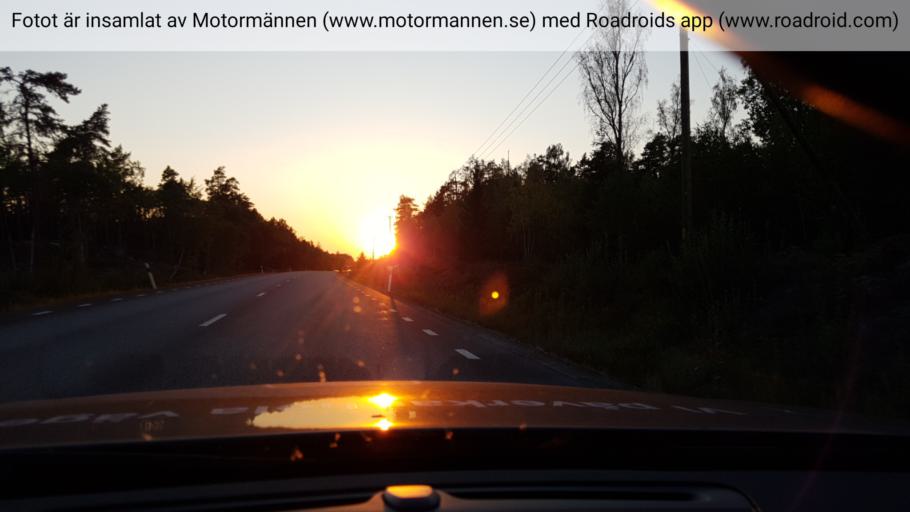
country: SE
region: Uppsala
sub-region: Osthammars Kommun
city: Bjorklinge
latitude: 59.9706
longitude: 17.3693
